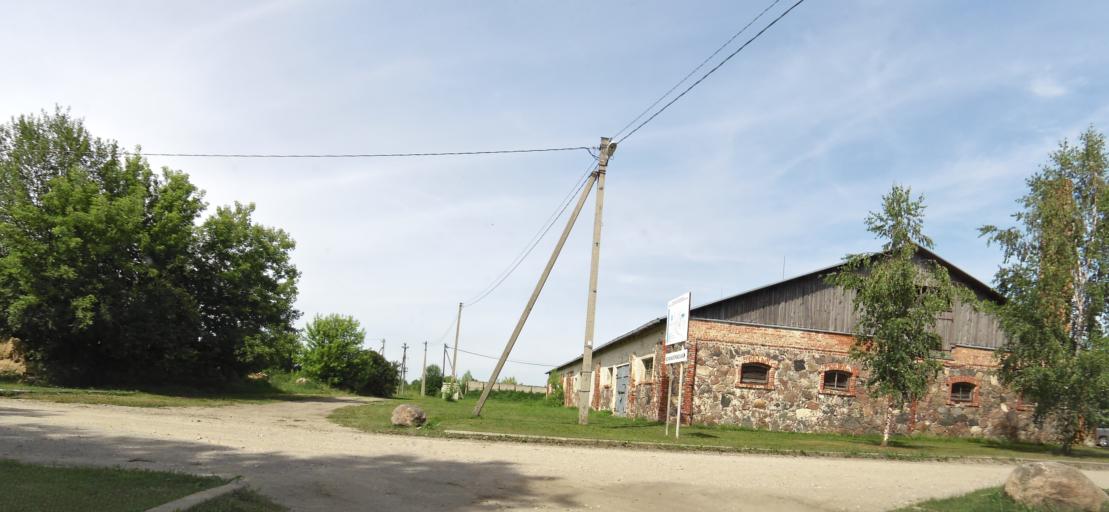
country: LT
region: Panevezys
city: Pasvalys
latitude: 55.9191
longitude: 24.2932
